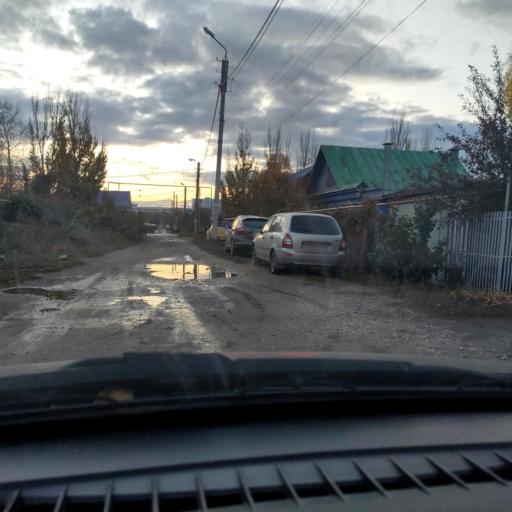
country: RU
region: Samara
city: Tol'yatti
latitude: 53.5391
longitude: 49.4173
